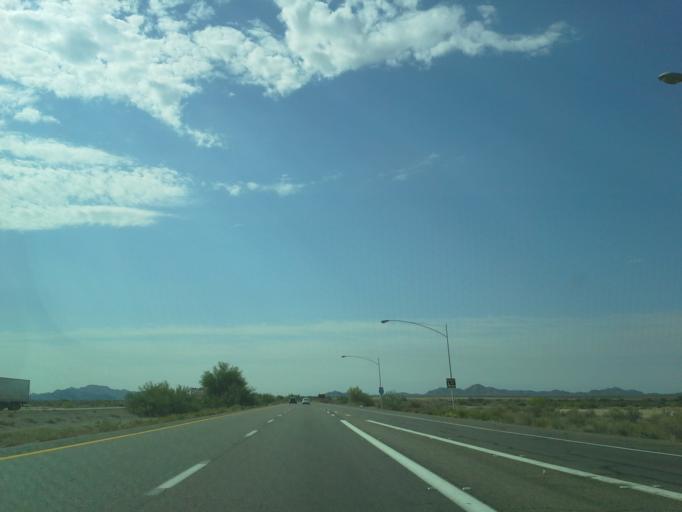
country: US
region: Arizona
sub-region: Pinal County
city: Casa Blanca
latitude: 33.1146
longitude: -111.8397
